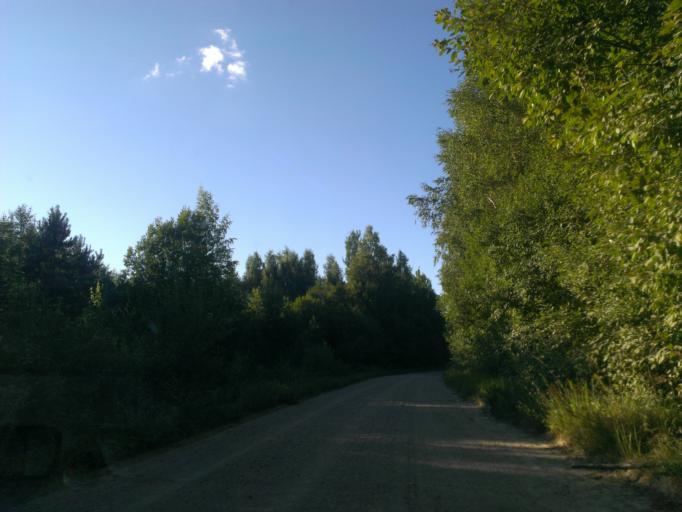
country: LV
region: Malpils
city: Malpils
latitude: 57.0989
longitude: 25.0433
